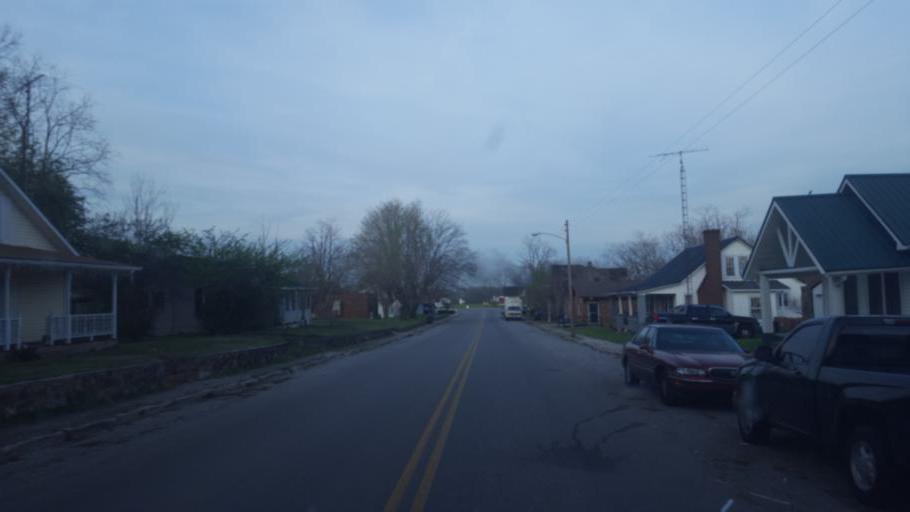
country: US
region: Kentucky
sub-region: Metcalfe County
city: Edmonton
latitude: 37.1414
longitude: -85.6951
